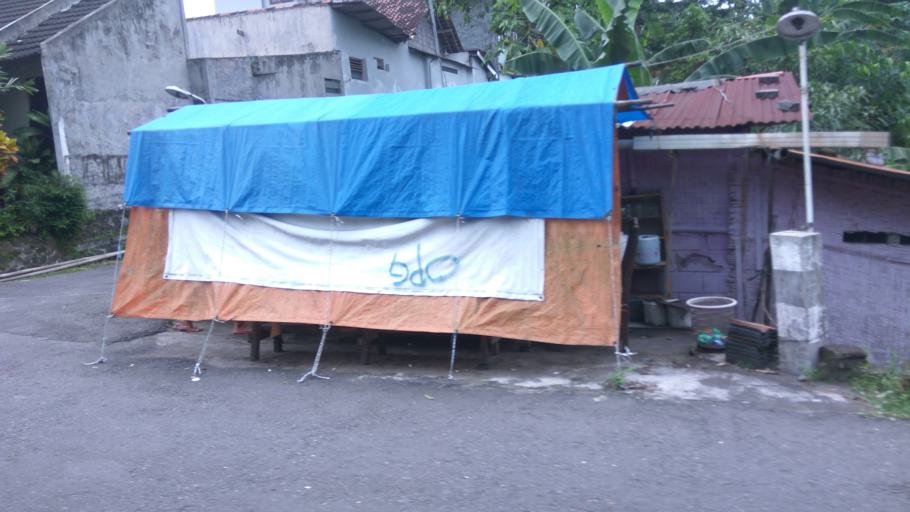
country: ID
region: Daerah Istimewa Yogyakarta
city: Depok
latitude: -7.7383
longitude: 110.4090
